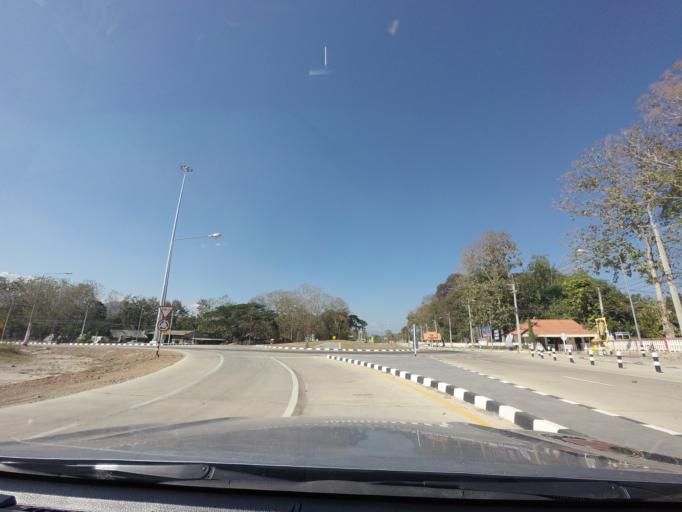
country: TH
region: Lampang
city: Chae Hom
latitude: 18.7278
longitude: 99.5840
